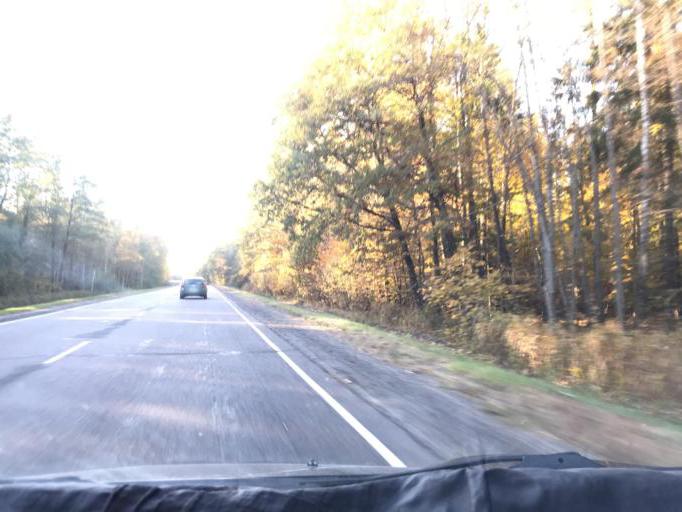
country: BY
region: Gomel
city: Pyetrykaw
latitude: 52.2704
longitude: 28.2789
